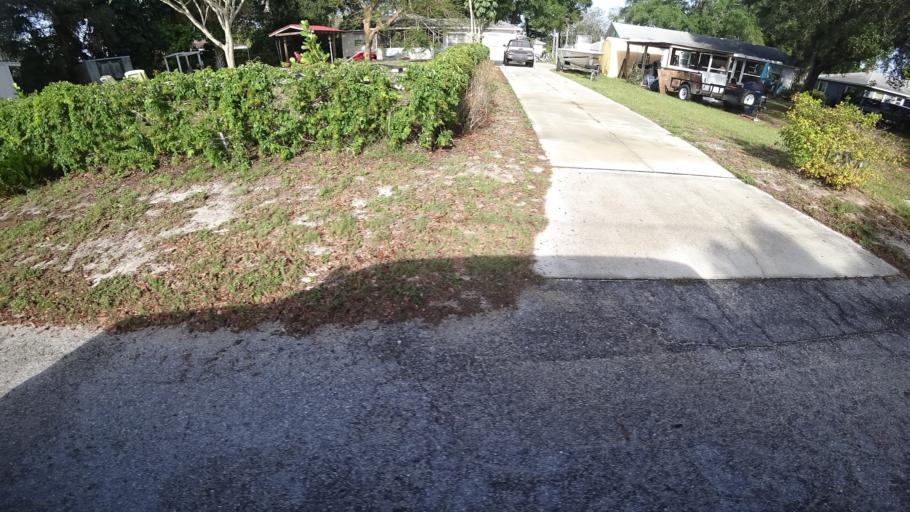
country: US
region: Florida
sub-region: Manatee County
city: West Bradenton
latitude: 27.5054
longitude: -82.6196
